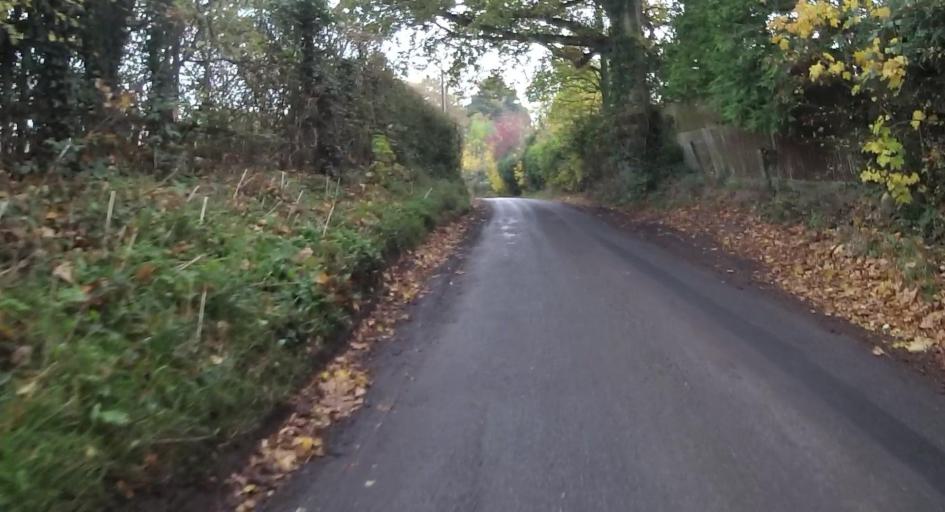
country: GB
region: England
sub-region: Wokingham
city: Finchampstead
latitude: 51.3673
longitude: -0.8604
